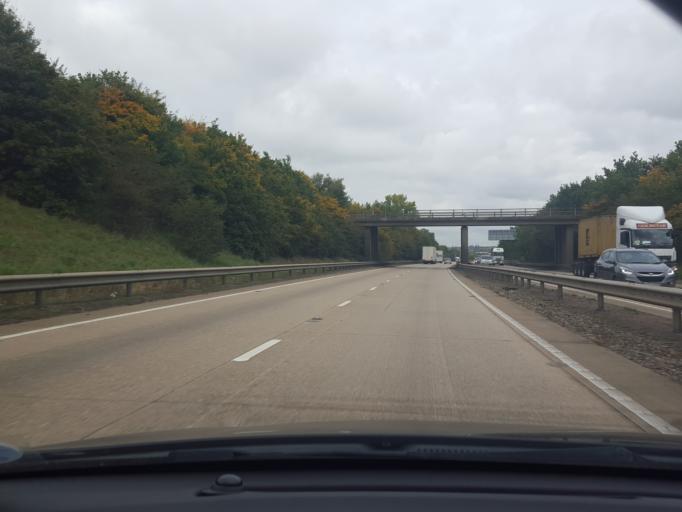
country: GB
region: England
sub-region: Suffolk
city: Bramford
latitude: 52.0488
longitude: 1.0972
